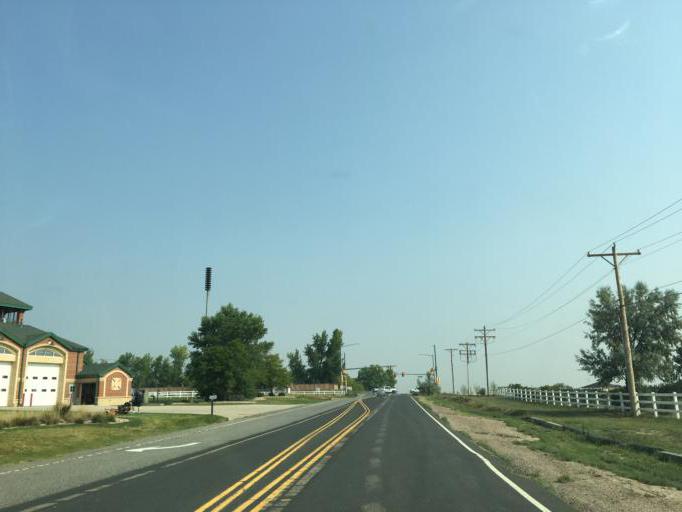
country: US
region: Colorado
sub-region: Adams County
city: Todd Creek
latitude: 39.9851
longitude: -104.8655
